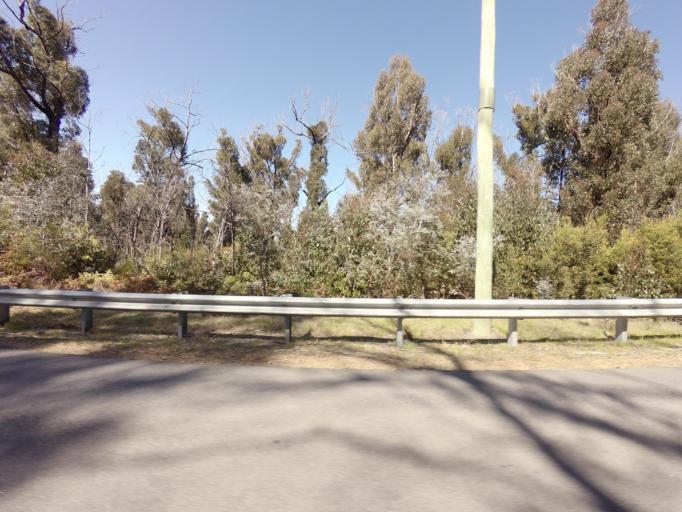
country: AU
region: Tasmania
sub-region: Derwent Valley
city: New Norfolk
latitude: -42.5520
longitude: 146.7135
